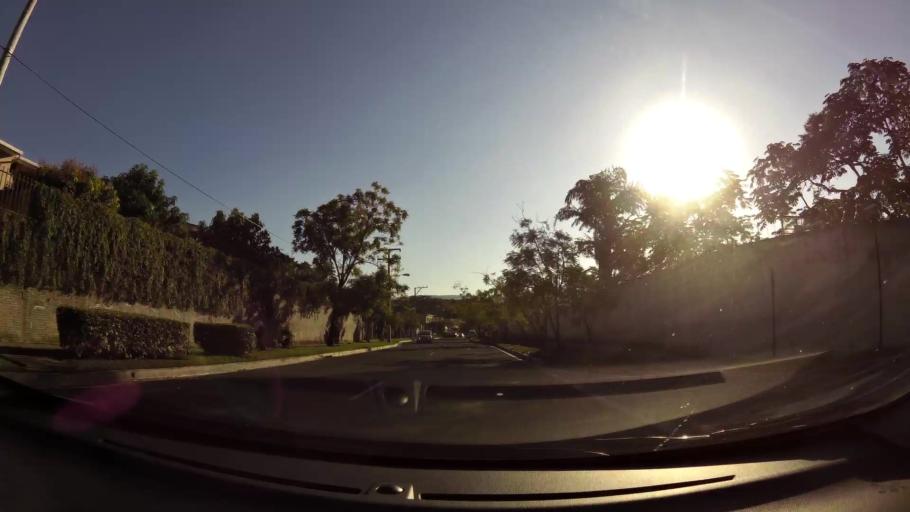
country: SV
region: La Libertad
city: Santa Tecla
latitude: 13.7400
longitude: -89.3569
